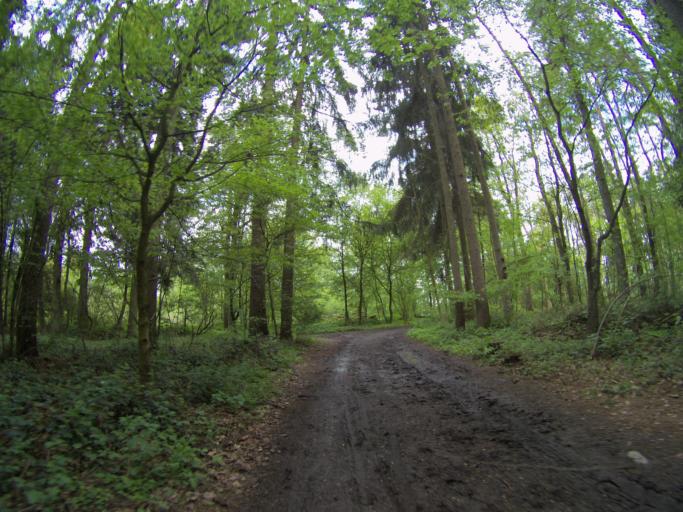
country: DE
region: Bavaria
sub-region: Upper Bavaria
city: Freising
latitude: 48.4158
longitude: 11.7619
